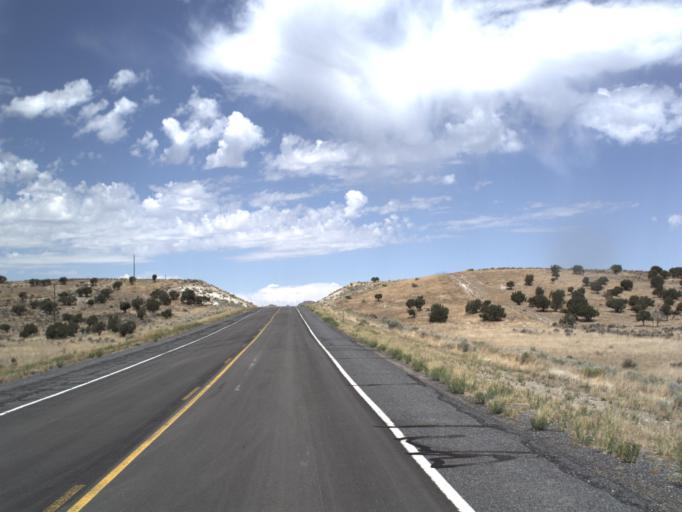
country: US
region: Utah
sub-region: Utah County
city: Eagle Mountain
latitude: 40.0646
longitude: -112.3201
